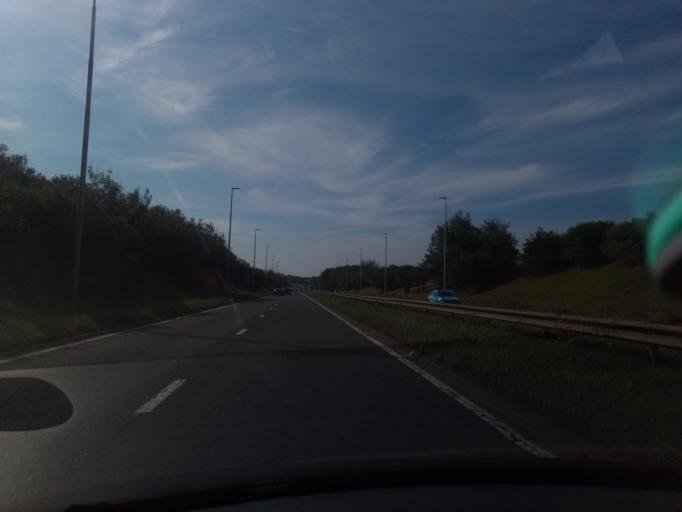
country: GB
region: England
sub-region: County Durham
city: Shotton
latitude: 54.7749
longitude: -1.3582
